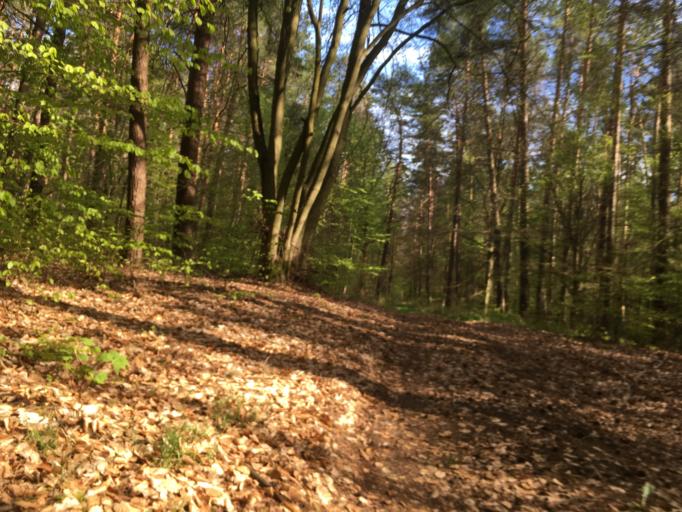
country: DE
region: Brandenburg
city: Bernau bei Berlin
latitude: 52.7196
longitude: 13.5625
